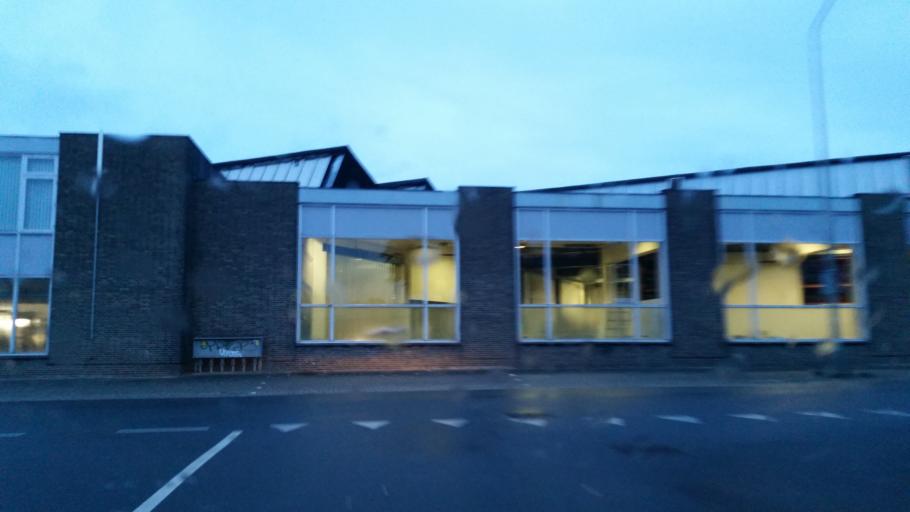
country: NL
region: Limburg
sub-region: Gemeente Maastricht
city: Maastricht
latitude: 50.8612
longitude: 5.6847
